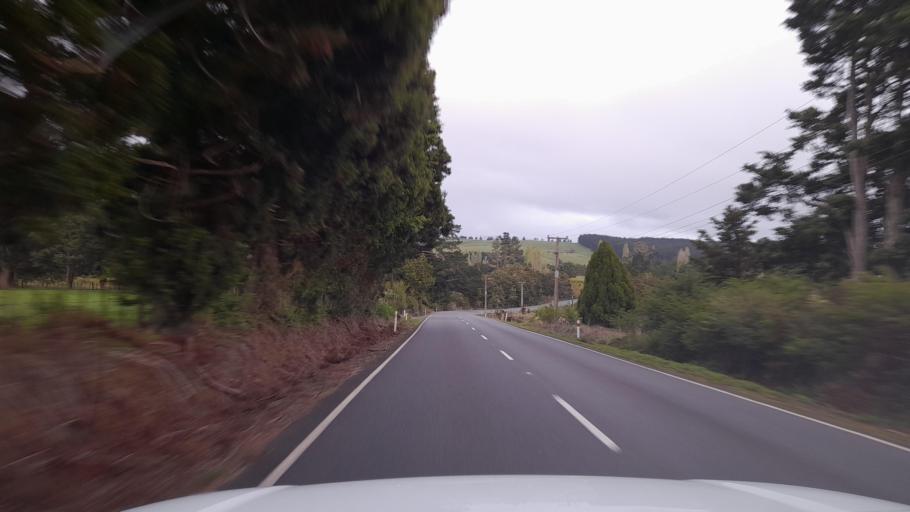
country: NZ
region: Northland
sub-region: Far North District
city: Waimate North
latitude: -35.5827
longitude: 173.8384
